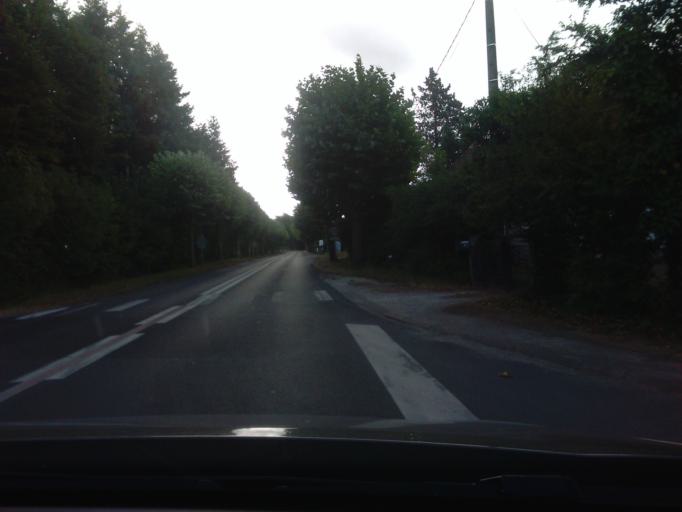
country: FR
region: Centre
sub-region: Departement du Loir-et-Cher
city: Cellettes
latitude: 47.5219
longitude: 1.3911
